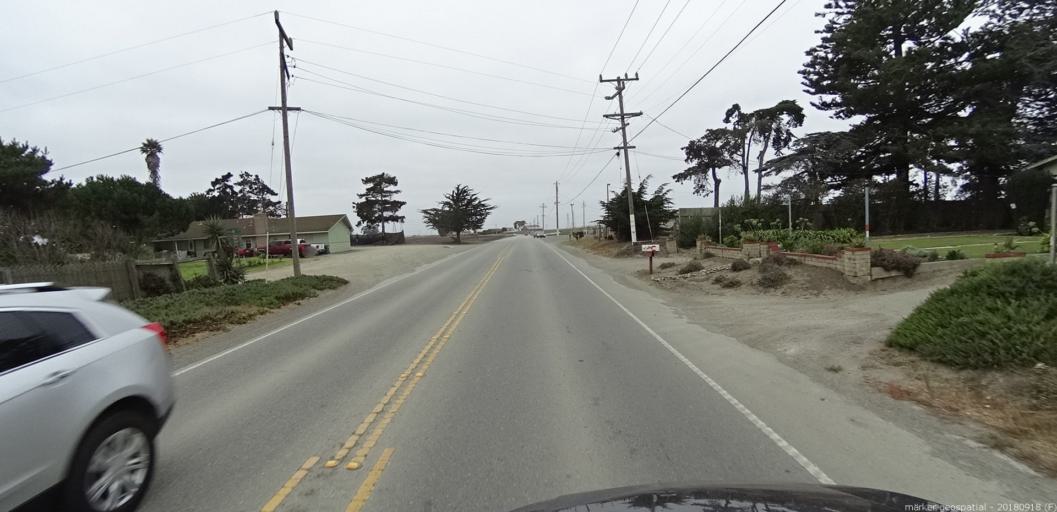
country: US
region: California
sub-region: Monterey County
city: Castroville
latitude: 36.7481
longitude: -121.7174
